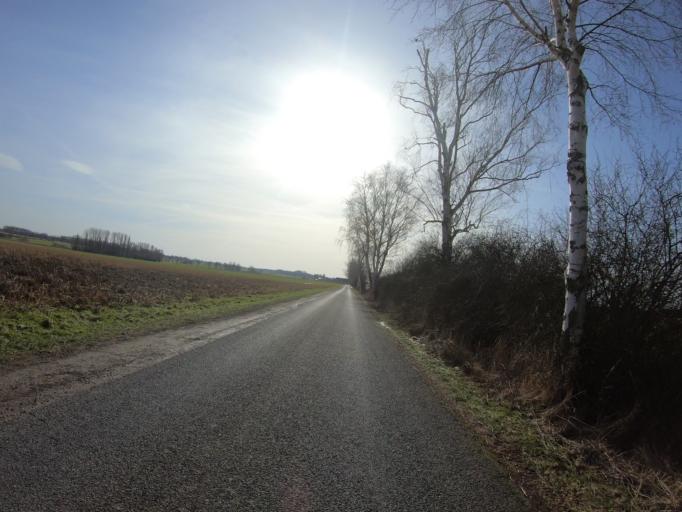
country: DE
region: Lower Saxony
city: Isenbuttel
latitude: 52.4161
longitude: 10.5646
